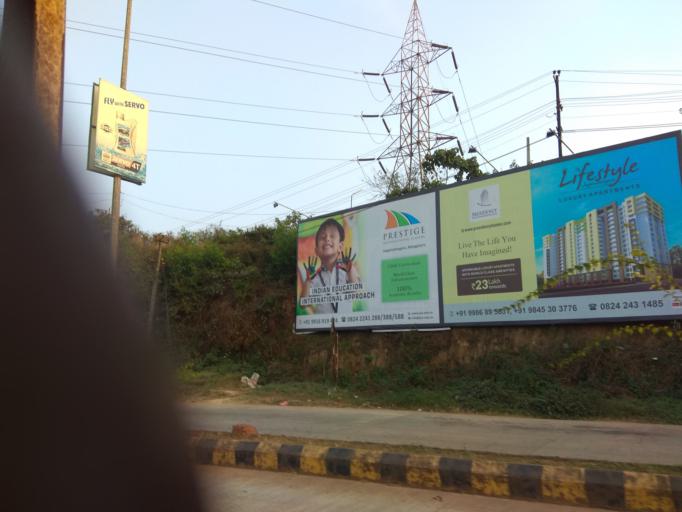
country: IN
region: Karnataka
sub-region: Dakshina Kannada
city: Mangalore
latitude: 12.9356
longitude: 74.8599
